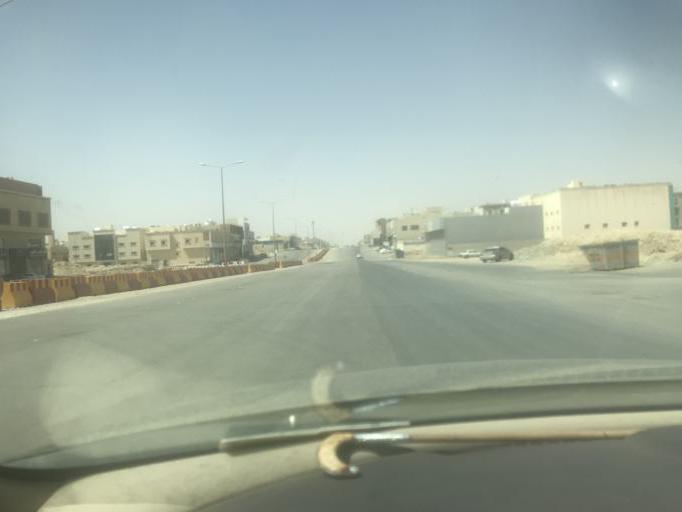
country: SA
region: Ar Riyad
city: Riyadh
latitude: 24.8143
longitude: 46.5987
